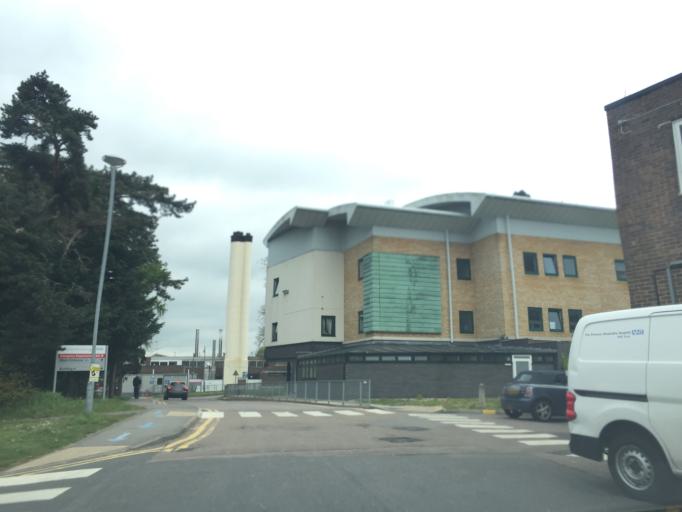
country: GB
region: England
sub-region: Essex
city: Harlow
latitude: 51.7715
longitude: 0.0853
